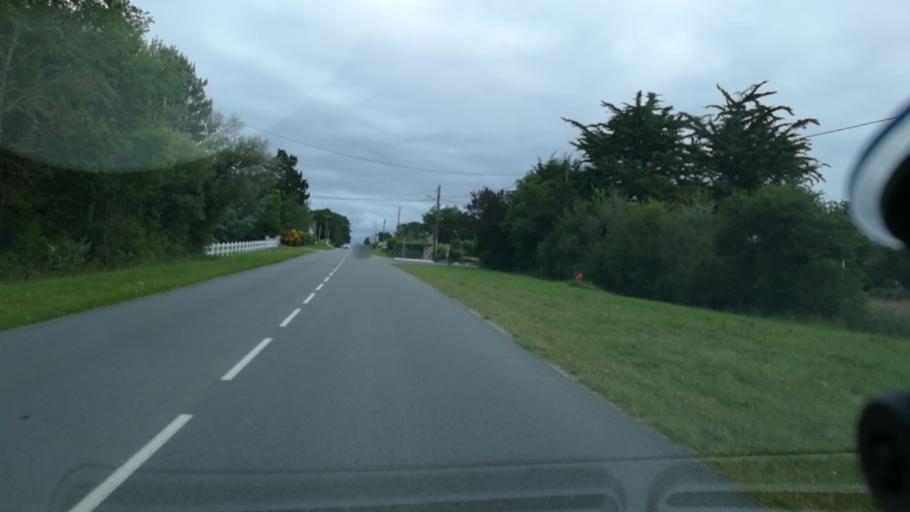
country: FR
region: Brittany
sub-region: Departement du Morbihan
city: Penestin
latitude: 47.4721
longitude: -2.4785
